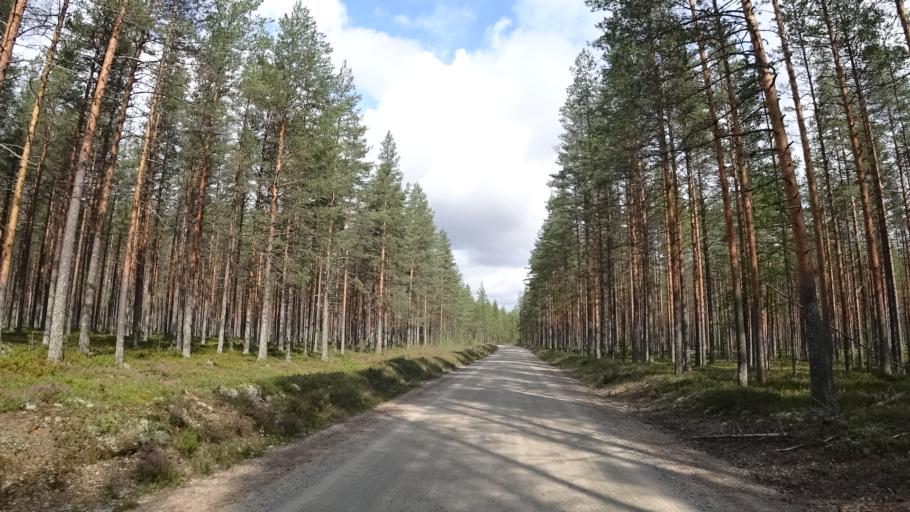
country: FI
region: North Karelia
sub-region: Joensuu
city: Ilomantsi
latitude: 62.9358
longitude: 31.4309
